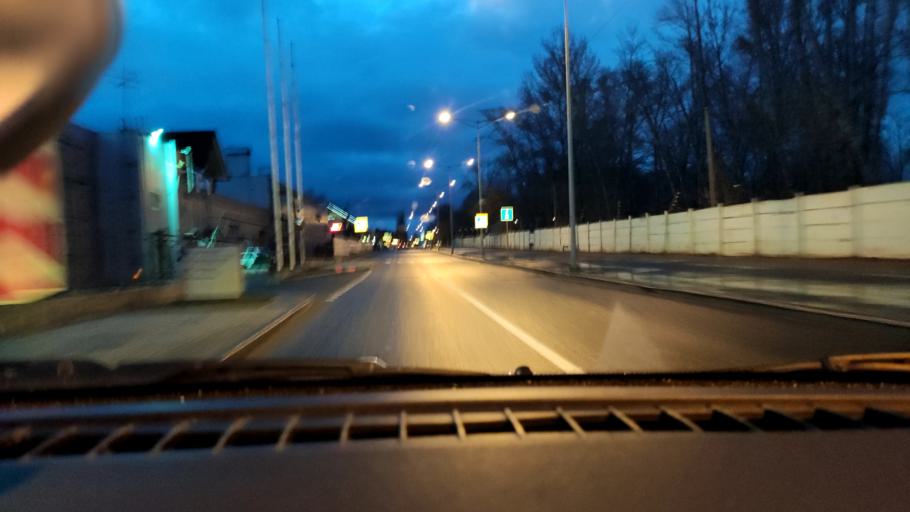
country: RU
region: Samara
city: Petra-Dubrava
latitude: 53.2917
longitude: 50.2861
